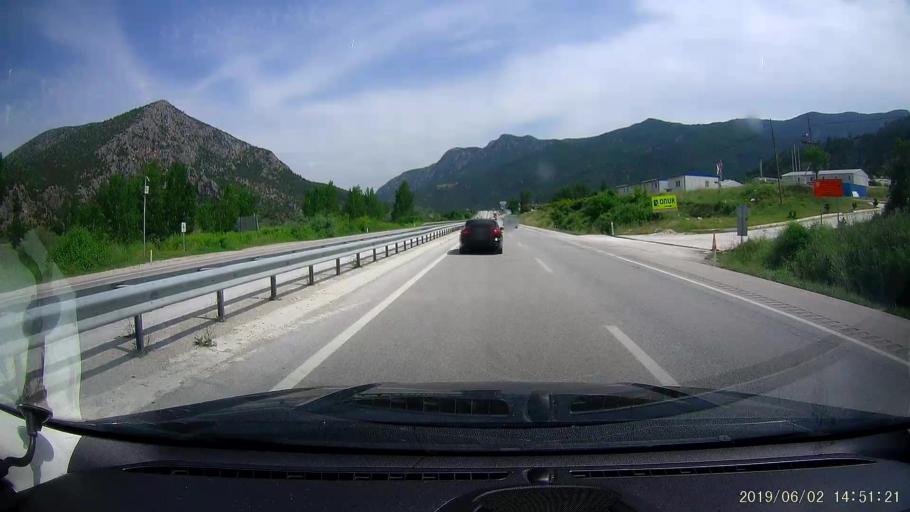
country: TR
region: Corum
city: Kargi
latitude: 41.0614
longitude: 34.5388
